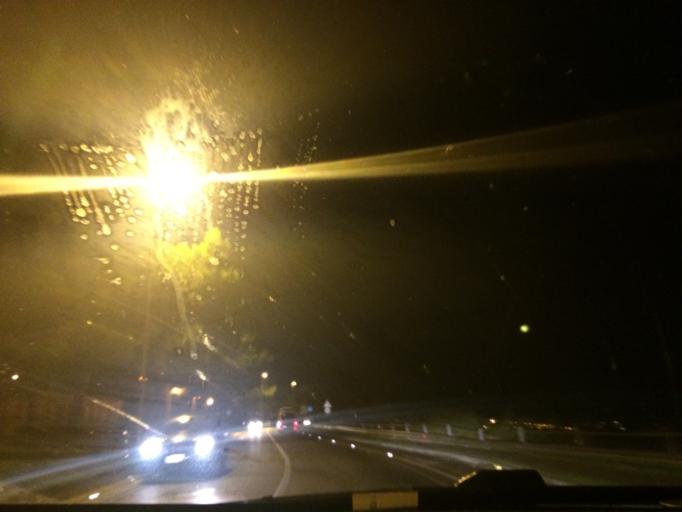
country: IT
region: Basilicate
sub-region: Provincia di Matera
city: Matera
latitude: 40.6586
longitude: 16.6031
